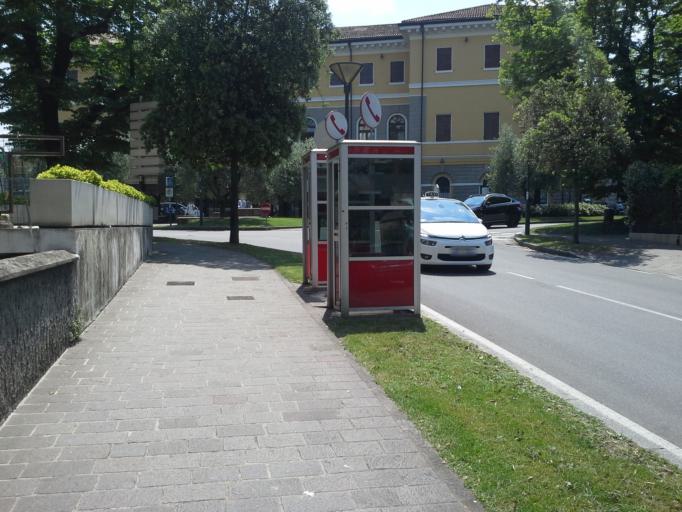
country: IT
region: Lombardy
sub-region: Provincia di Brescia
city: Desenzano del Garda
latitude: 45.4633
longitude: 10.5366
